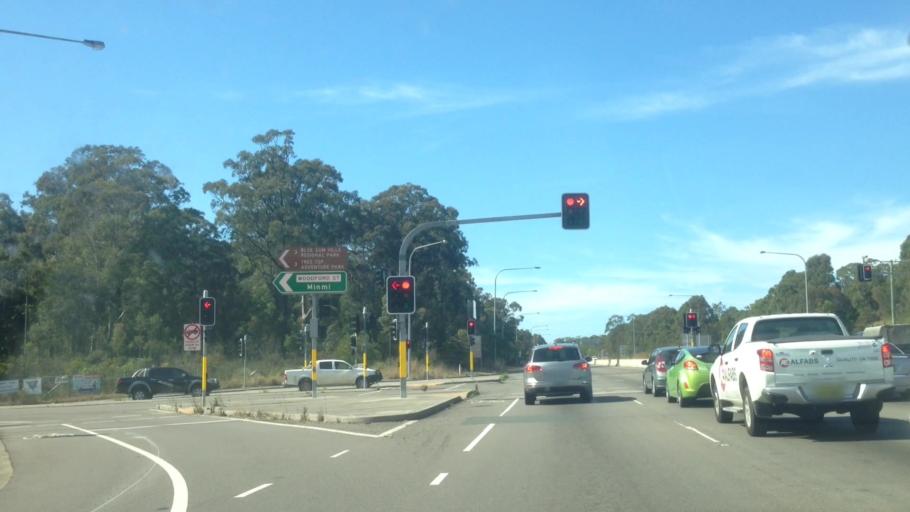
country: AU
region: New South Wales
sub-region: Lake Macquarie Shire
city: Holmesville
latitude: -32.8941
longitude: 151.6069
